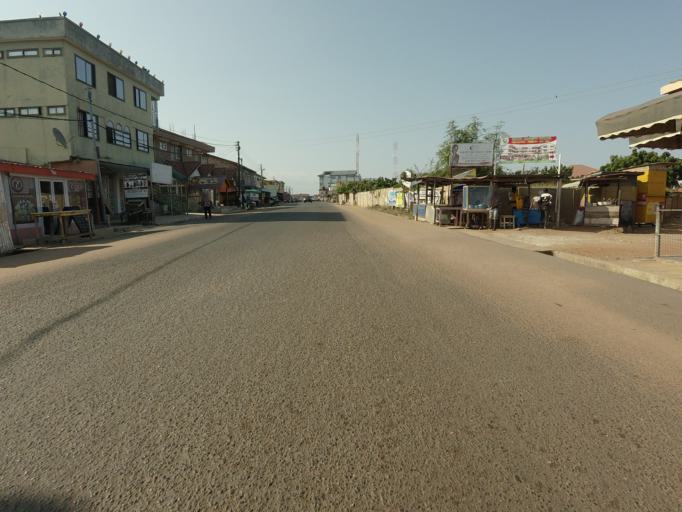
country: GH
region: Greater Accra
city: Nungua
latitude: 5.6267
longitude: -0.0905
